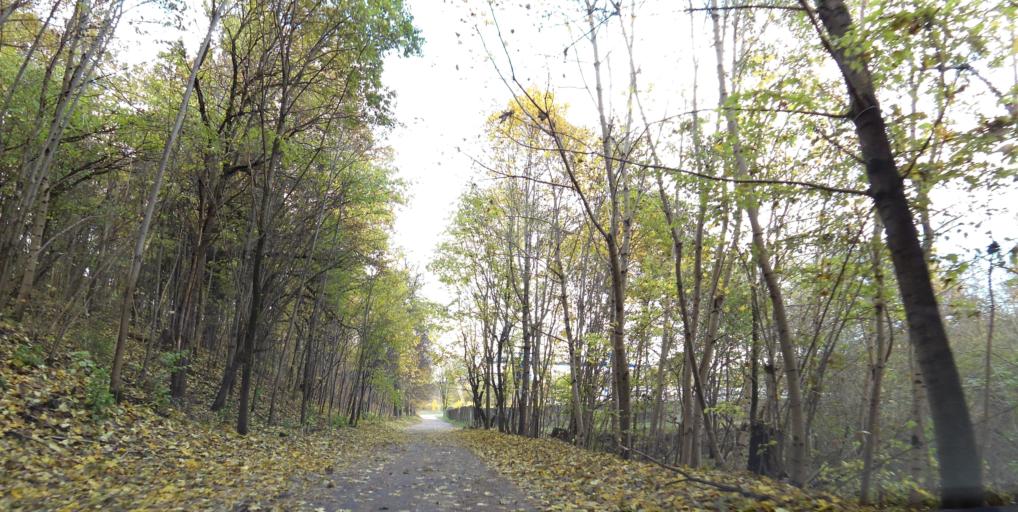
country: LT
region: Vilnius County
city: Vilkpede
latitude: 54.6592
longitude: 25.2591
